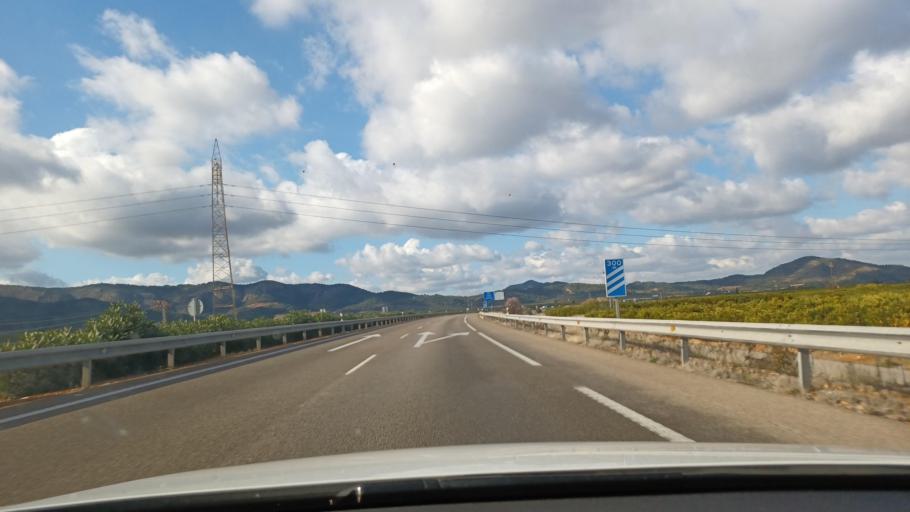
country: ES
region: Valencia
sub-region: Provincia de Castello
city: Villavieja
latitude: 39.8704
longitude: -0.1844
